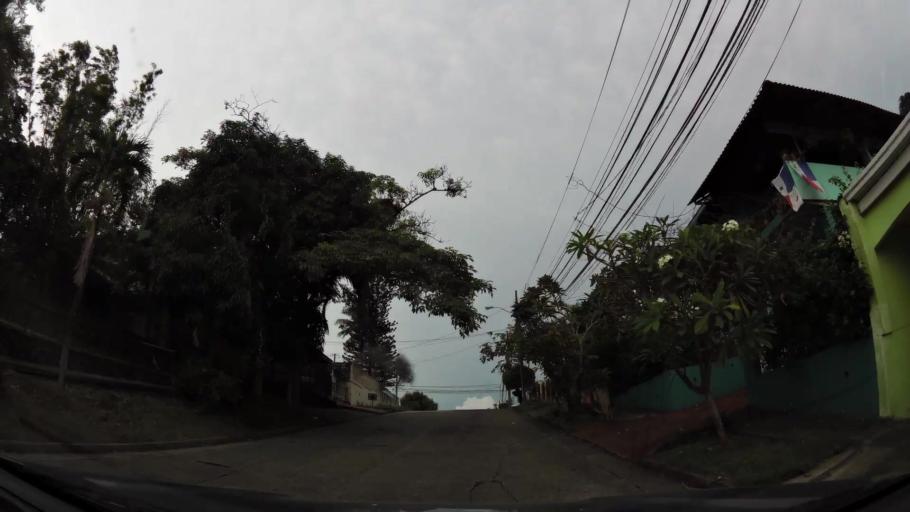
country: PA
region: Panama
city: Panama
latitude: 9.0152
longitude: -79.5262
